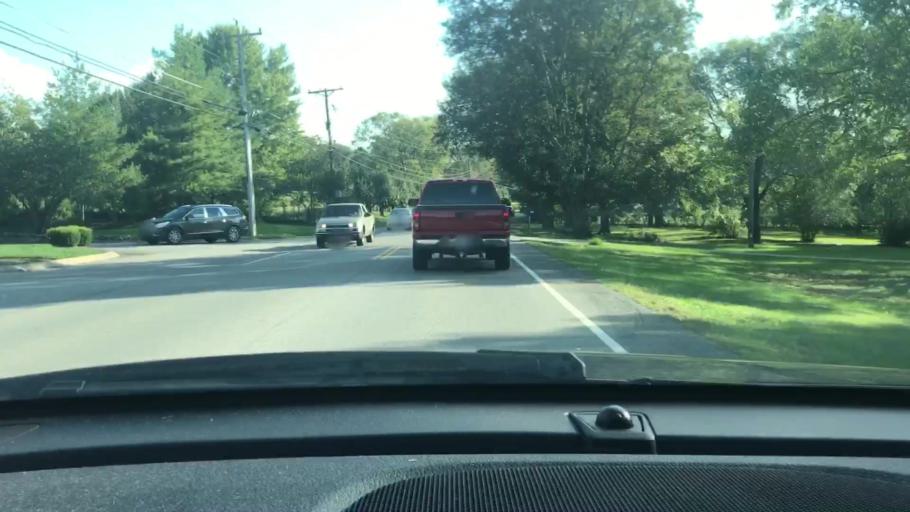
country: US
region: Tennessee
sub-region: Sumner County
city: Shackle Island
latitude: 36.3493
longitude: -86.6127
